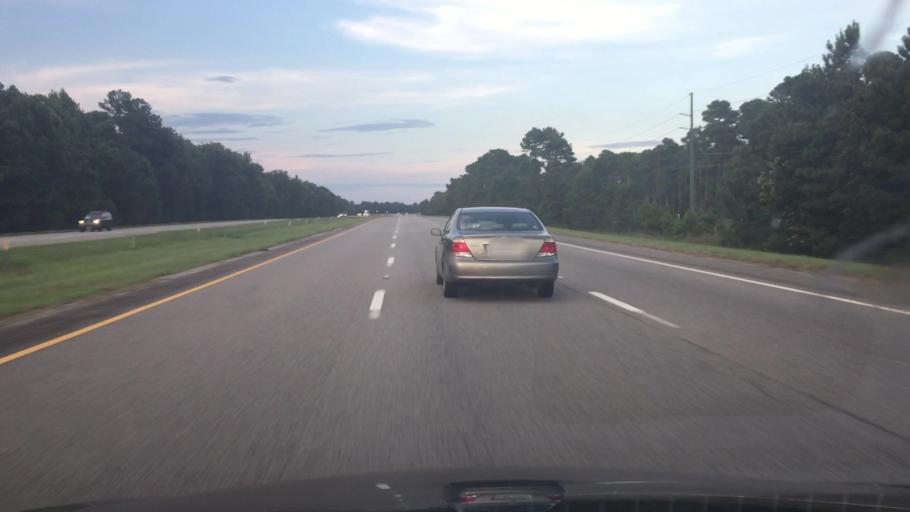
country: US
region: South Carolina
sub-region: Horry County
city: Forestbrook
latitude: 33.7481
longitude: -78.9079
